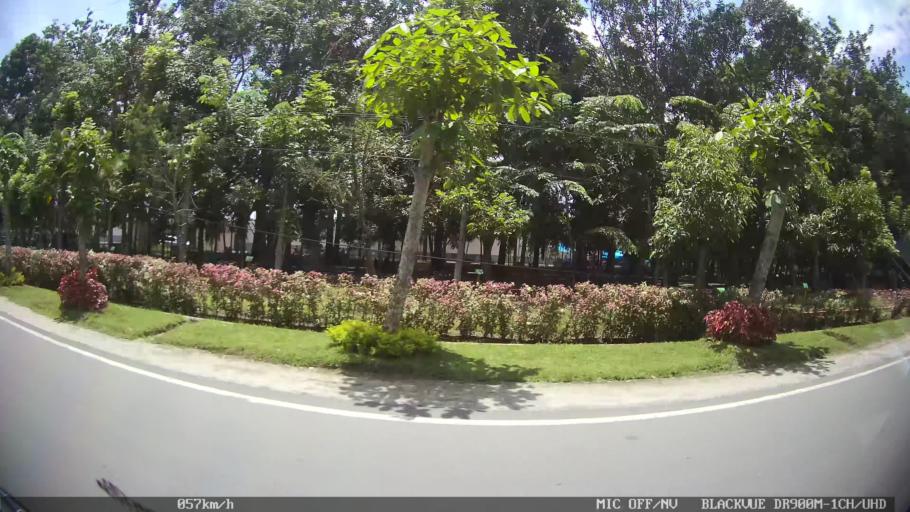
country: ID
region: North Sumatra
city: Percut
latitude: 3.5503
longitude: 98.8654
